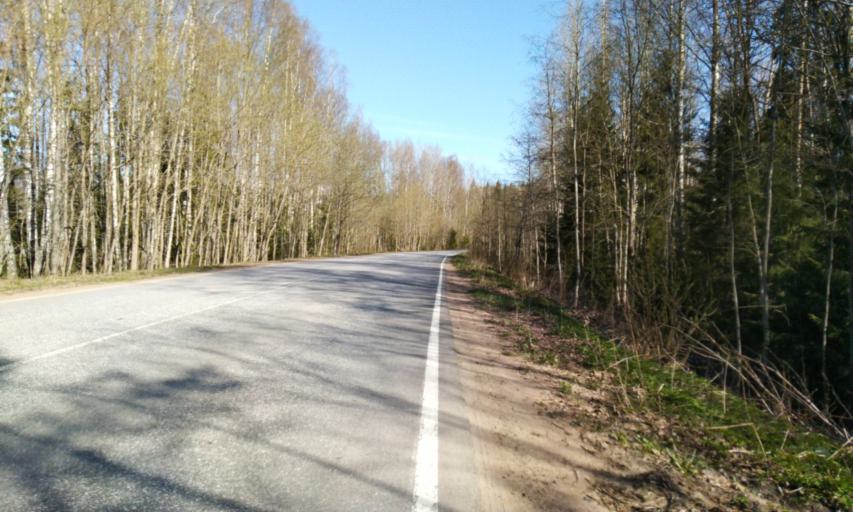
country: RU
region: Leningrad
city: Garbolovo
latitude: 60.3673
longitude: 30.4411
